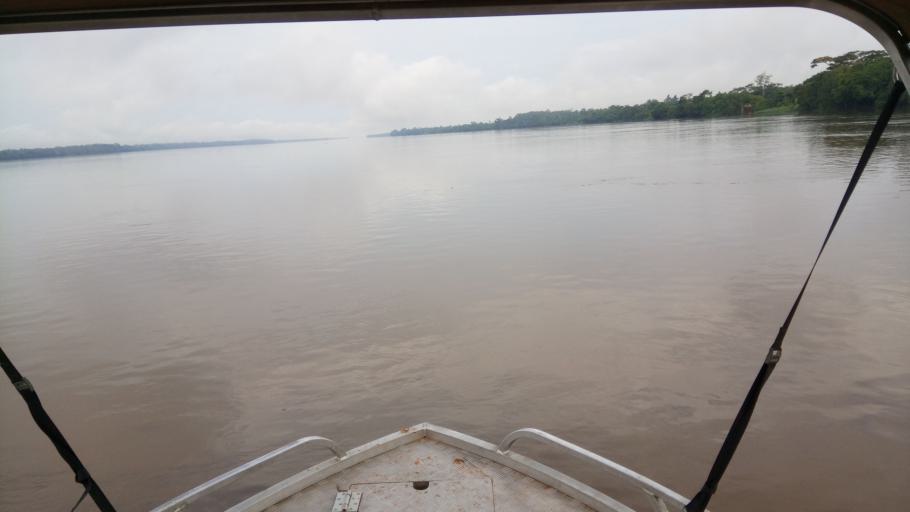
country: CD
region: Eastern Province
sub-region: Sous-Region de la Tshopo
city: Yangambi
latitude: 0.6149
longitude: 24.7162
